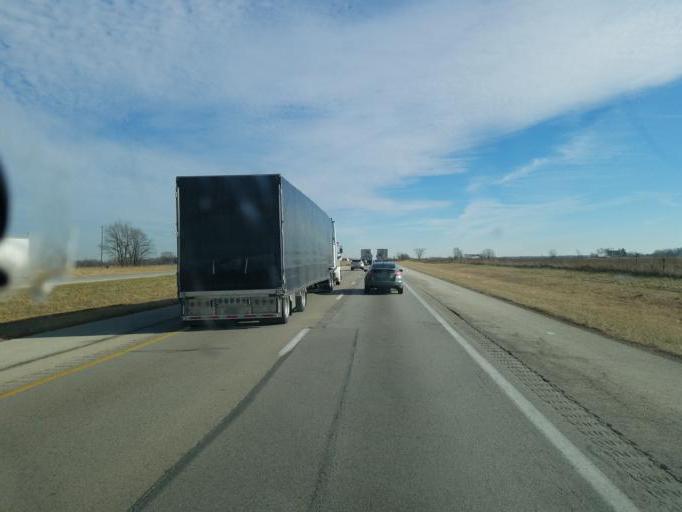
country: US
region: Ohio
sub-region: Preble County
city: Lewisburg
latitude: 39.8355
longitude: -84.6111
